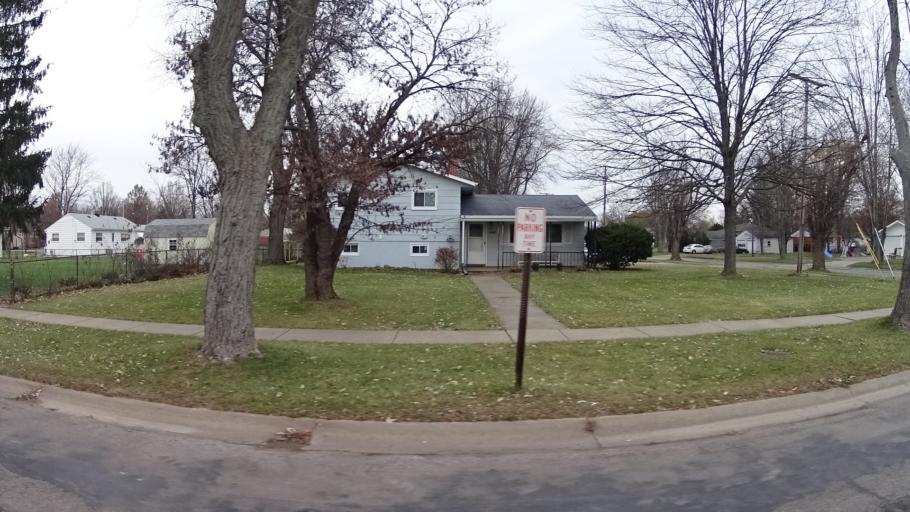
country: US
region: Ohio
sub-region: Lorain County
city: North Ridgeville
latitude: 41.3983
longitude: -82.0056
